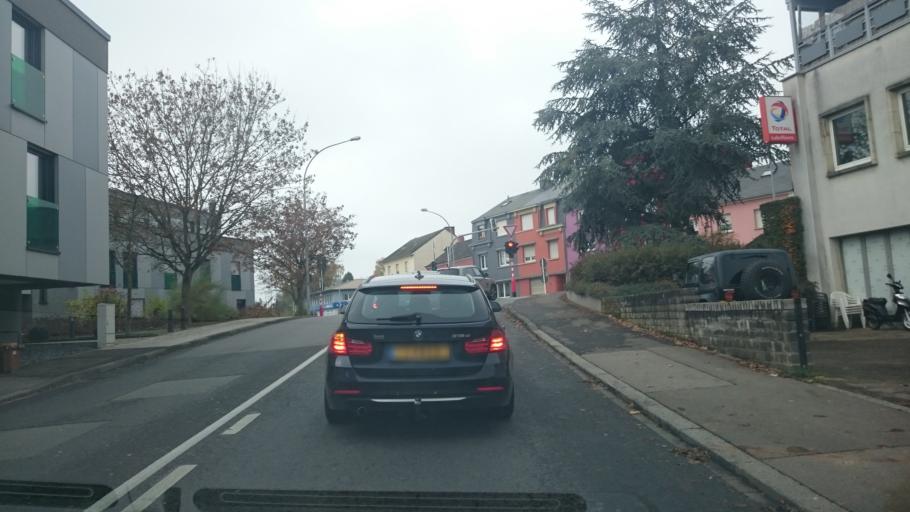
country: LU
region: Luxembourg
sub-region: Canton de Luxembourg
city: Strassen
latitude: 49.6029
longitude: 6.0918
